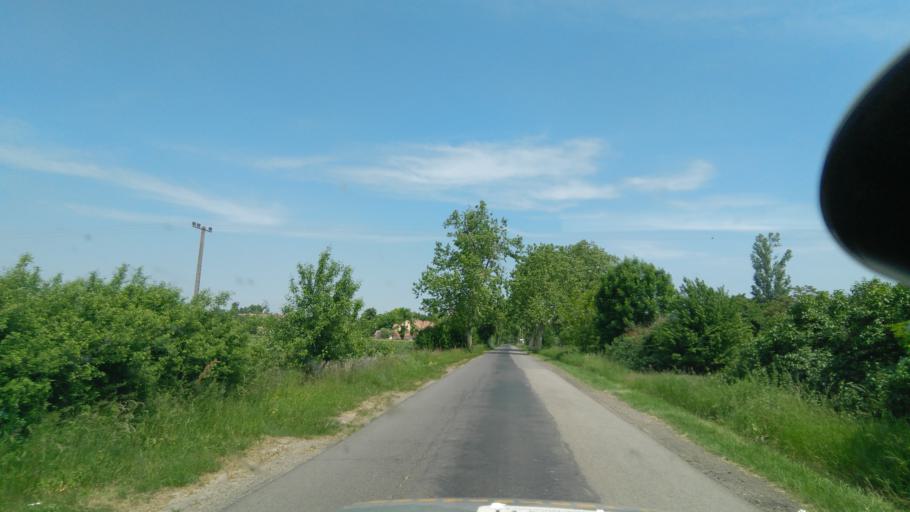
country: HU
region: Csongrad
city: Fabiansebestyen
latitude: 46.5841
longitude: 20.4689
